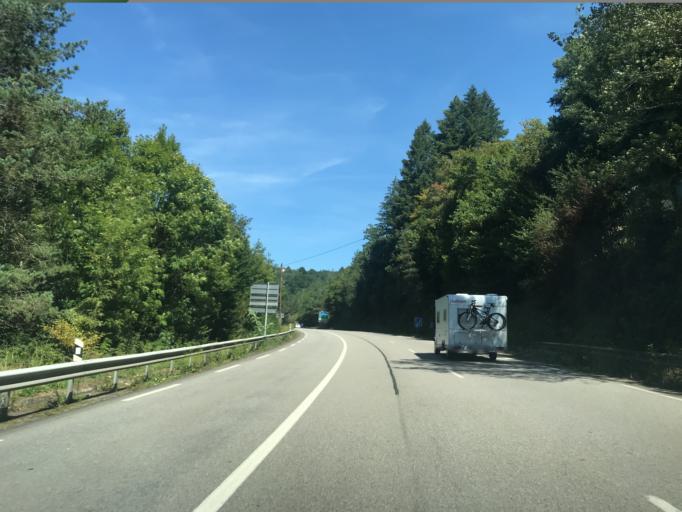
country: FR
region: Limousin
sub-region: Departement de la Correze
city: Laguenne
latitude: 45.2509
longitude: 1.7758
